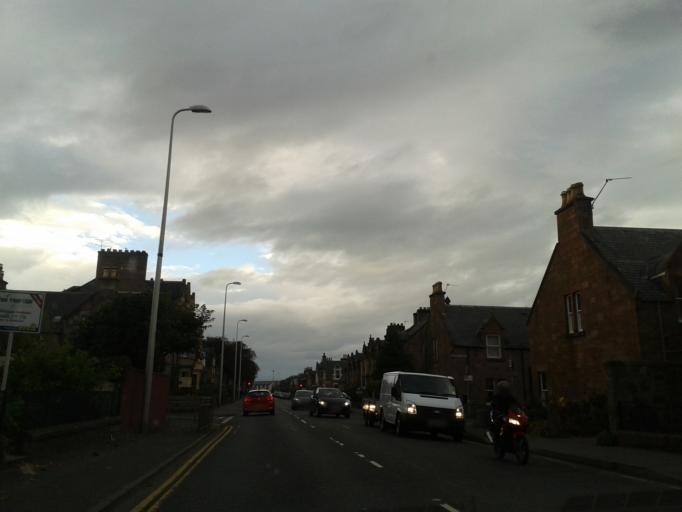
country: GB
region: Scotland
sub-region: Highland
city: Inverness
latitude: 57.4767
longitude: -4.2318
